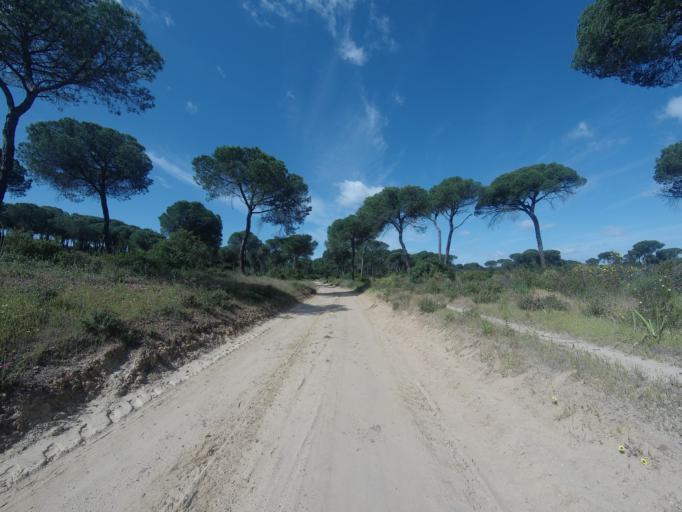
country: ES
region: Andalusia
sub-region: Provincia de Huelva
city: Aljaraque
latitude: 37.2358
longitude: -7.0580
